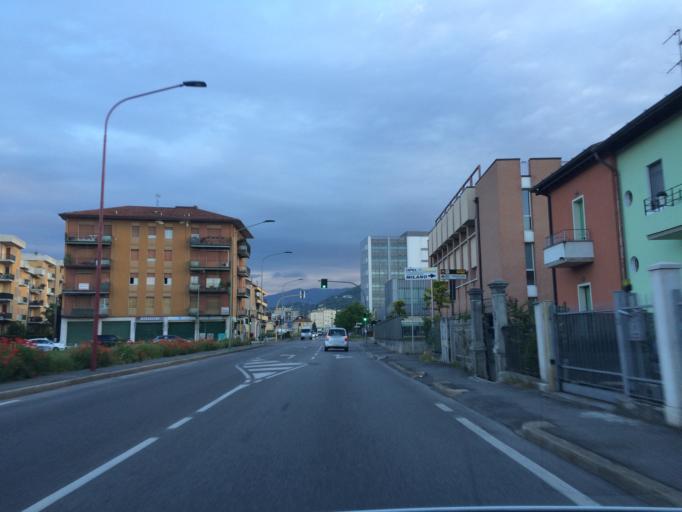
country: IT
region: Lombardy
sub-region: Provincia di Brescia
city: Brescia
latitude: 45.5194
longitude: 10.2289
